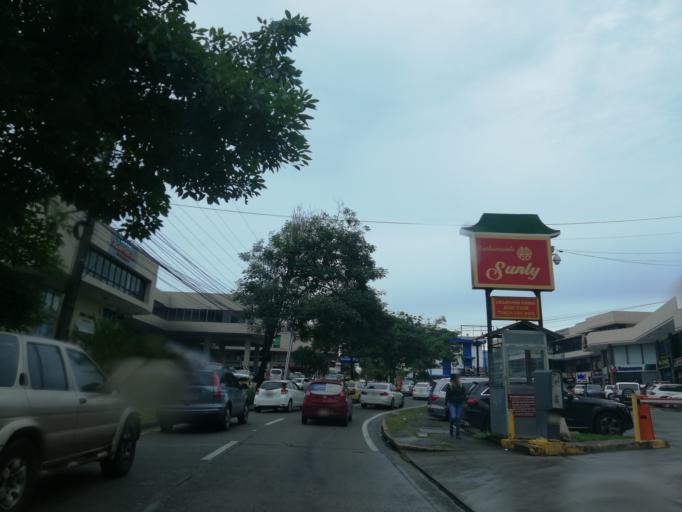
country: PA
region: Panama
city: Panama
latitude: 9.0067
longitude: -79.5374
